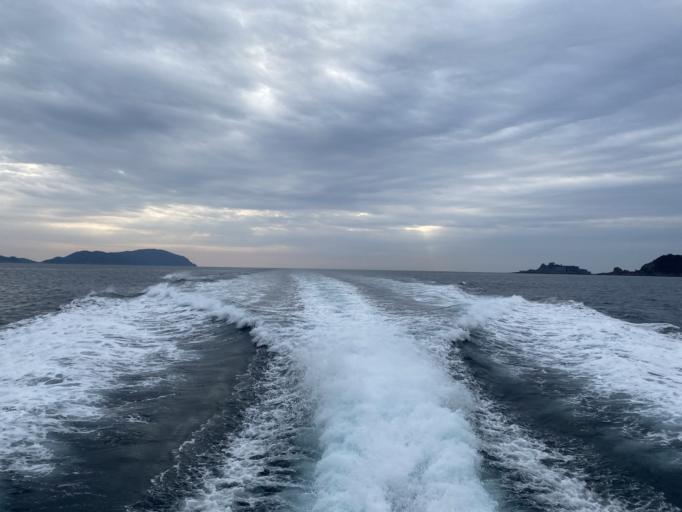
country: JP
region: Nagasaki
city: Nagasaki-shi
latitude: 32.6403
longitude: 129.7619
